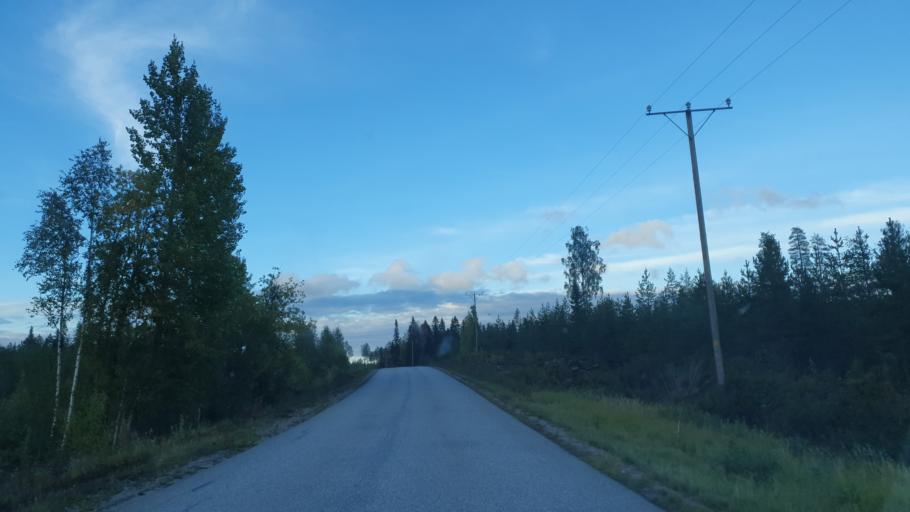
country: FI
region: Kainuu
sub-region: Kehys-Kainuu
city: Kuhmo
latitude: 64.4186
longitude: 29.9628
